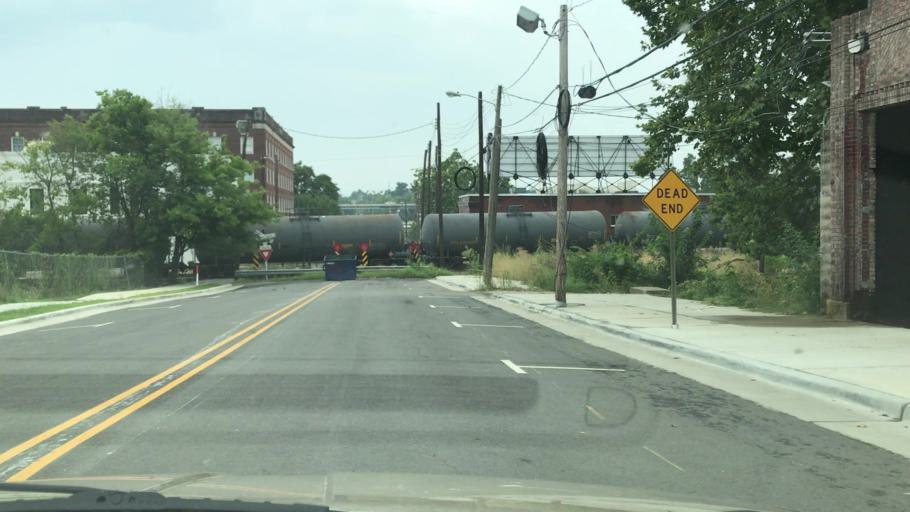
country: US
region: Louisiana
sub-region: Caddo Parish
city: Shreveport
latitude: 32.5088
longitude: -93.7490
